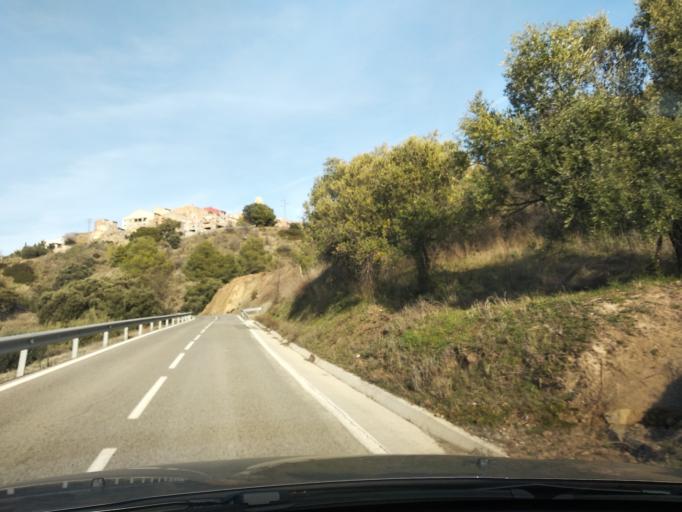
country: ES
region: Catalonia
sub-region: Provincia de Tarragona
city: Margalef
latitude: 41.2231
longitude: 0.7767
